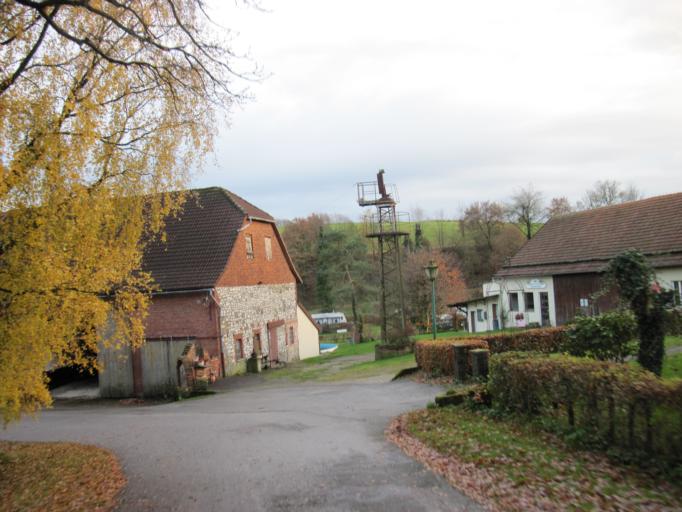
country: DE
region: North Rhine-Westphalia
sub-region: Regierungsbezirk Detmold
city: Altenbeken
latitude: 51.8041
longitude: 8.9423
